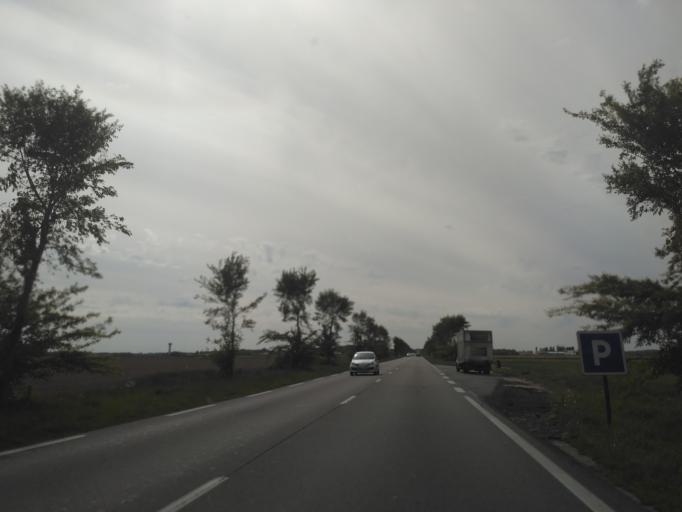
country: FR
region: Ile-de-France
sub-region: Departement de Seine-et-Marne
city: Soignolles-en-Brie
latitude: 48.6322
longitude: 2.6890
